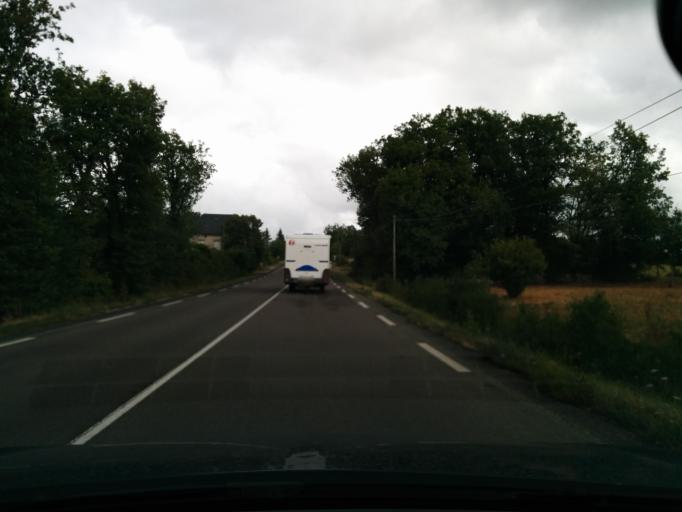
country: FR
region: Midi-Pyrenees
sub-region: Departement du Lot
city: Souillac
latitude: 45.0044
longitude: 1.5180
